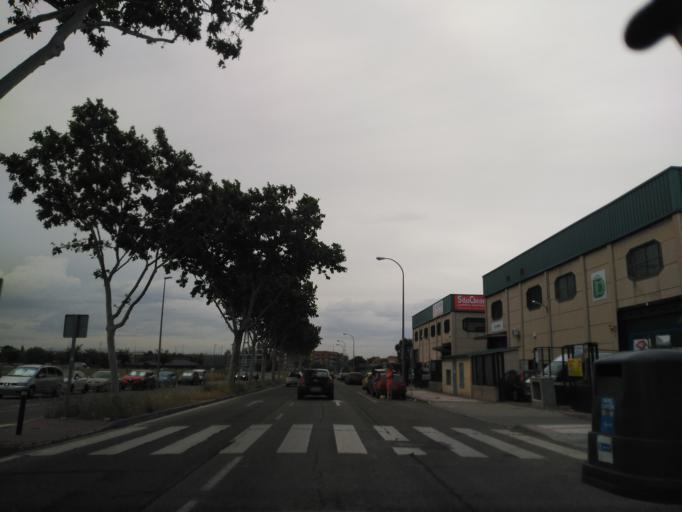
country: ES
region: Madrid
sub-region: Provincia de Madrid
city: Villaverde
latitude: 40.3391
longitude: -3.7153
